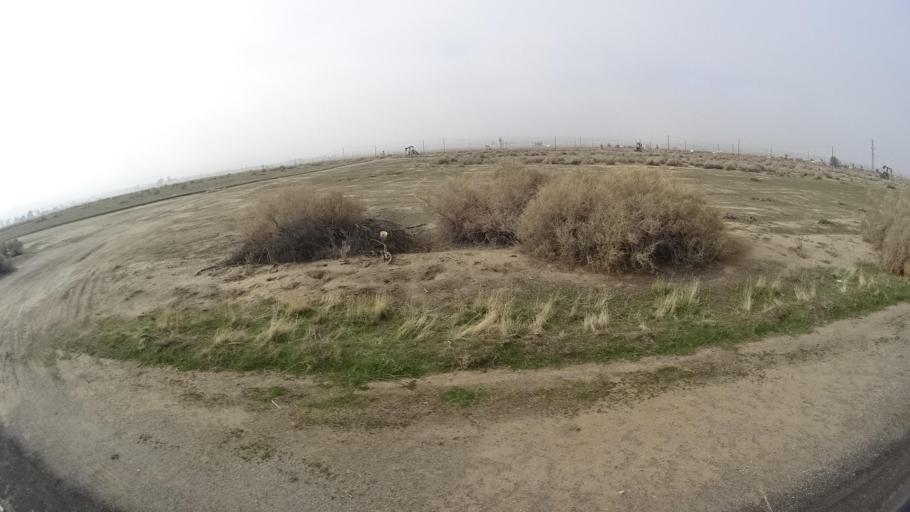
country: US
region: California
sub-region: Kern County
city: Maricopa
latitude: 35.0528
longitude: -119.3492
